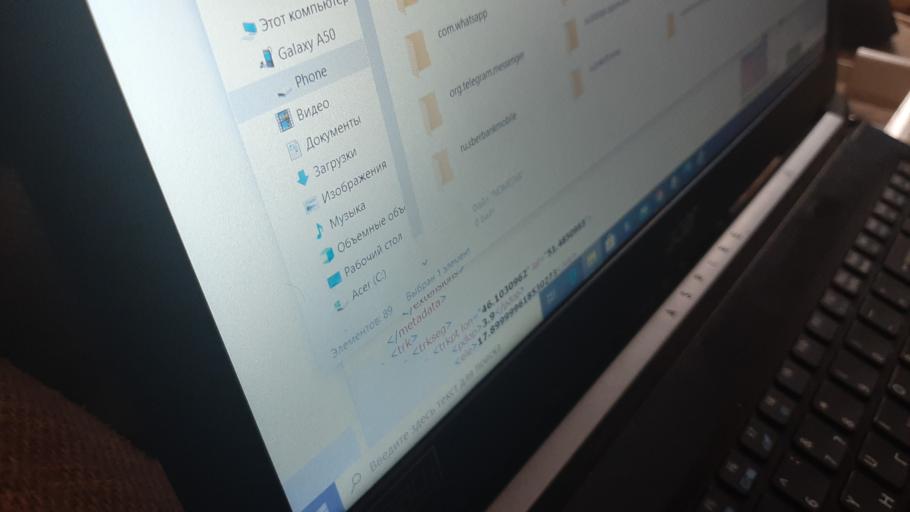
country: RU
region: Saratov
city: Engel's
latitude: 51.5009
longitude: 46.1173
